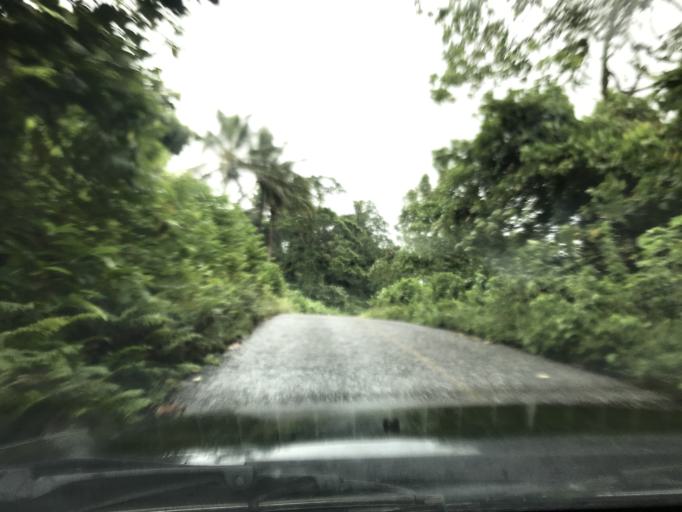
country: SB
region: Western Province
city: Gizo
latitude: -8.2645
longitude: 157.2357
